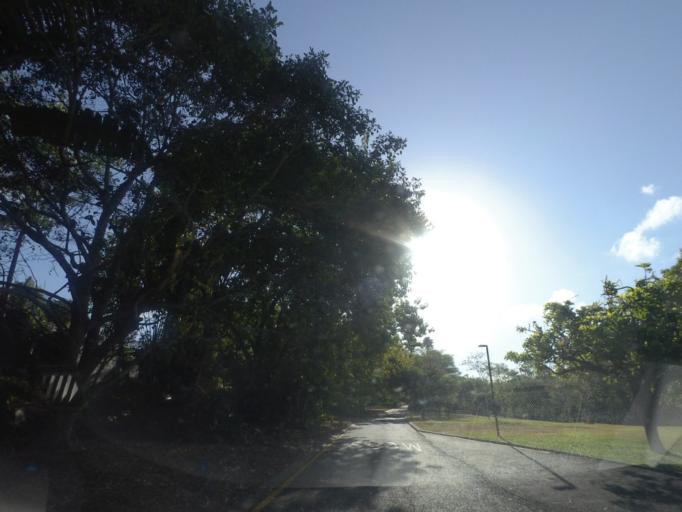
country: AU
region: Queensland
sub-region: Brisbane
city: Taringa
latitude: -27.4776
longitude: 152.9769
